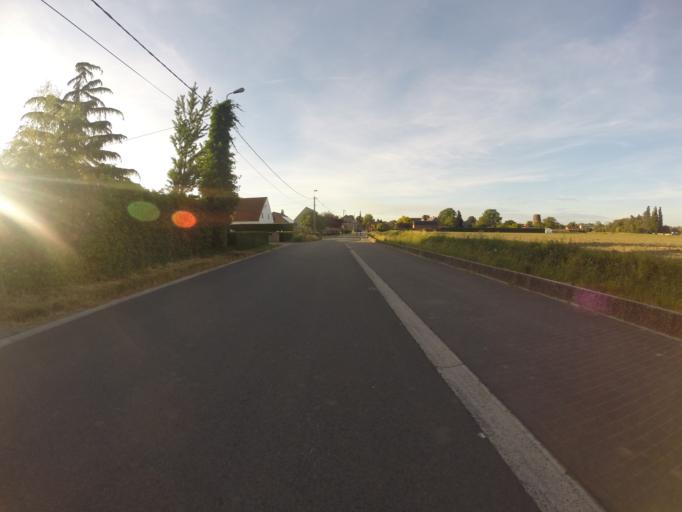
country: BE
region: Flanders
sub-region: Provincie Oost-Vlaanderen
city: Aalter
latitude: 51.1249
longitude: 3.4844
